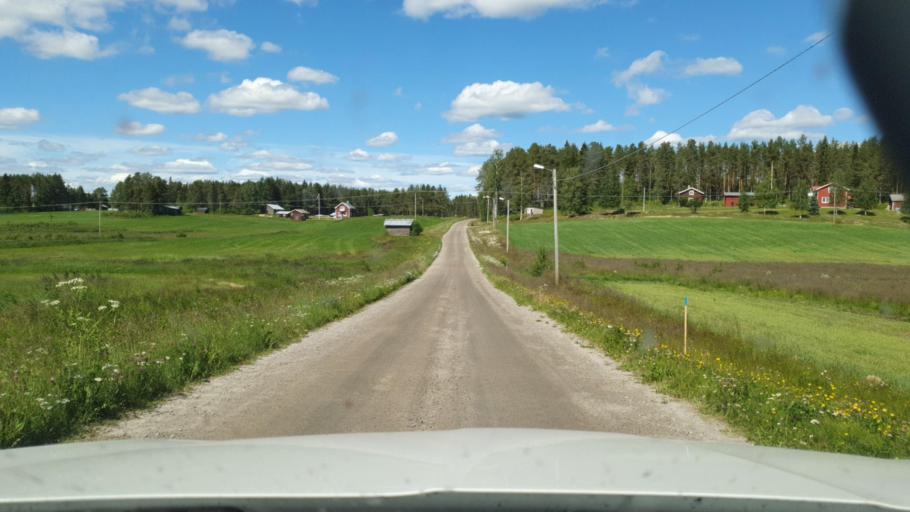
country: SE
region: Vaesterbotten
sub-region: Skelleftea Kommun
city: Byske
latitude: 65.1207
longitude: 21.2102
